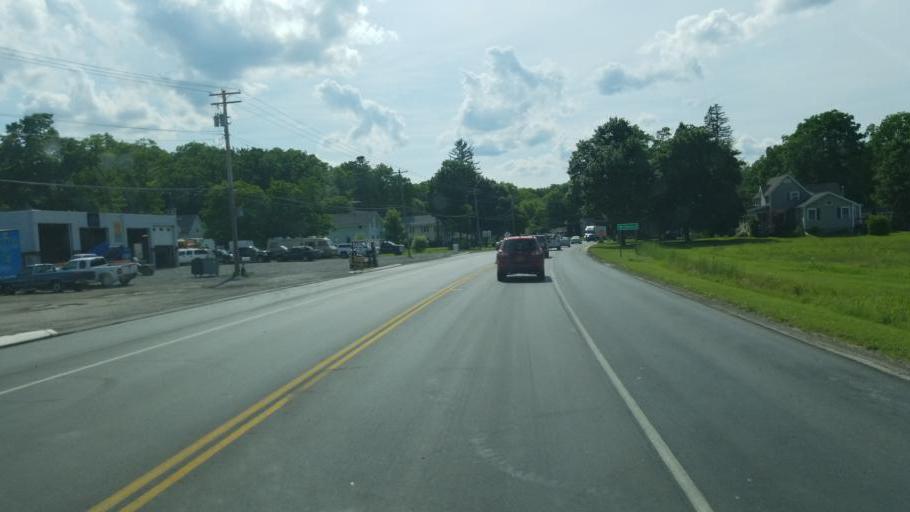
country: US
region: New York
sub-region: Ontario County
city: Clifton Springs
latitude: 42.8577
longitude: -77.1047
